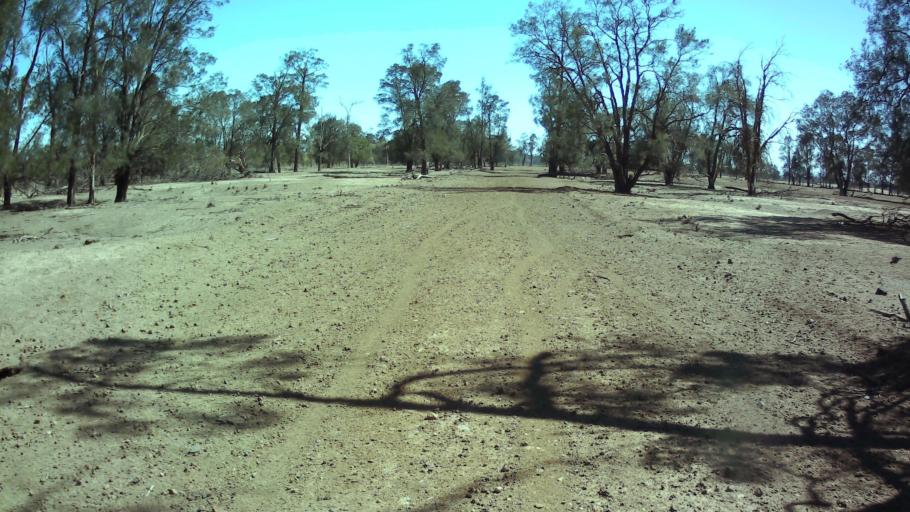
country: AU
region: New South Wales
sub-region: Bland
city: West Wyalong
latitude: -33.7607
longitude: 147.6586
